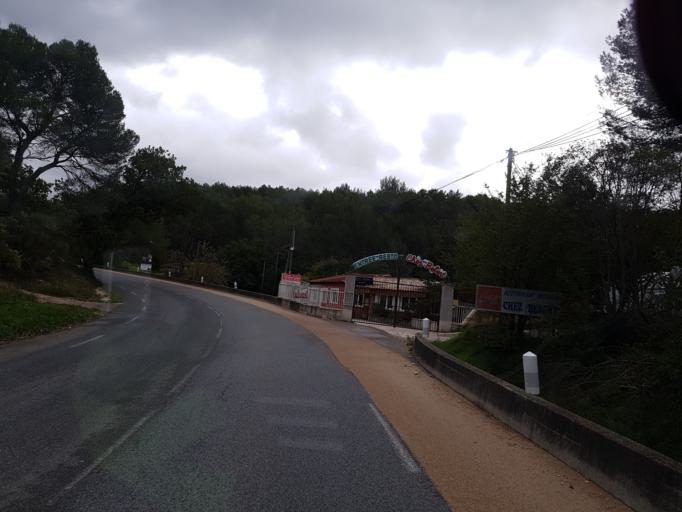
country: FR
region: Provence-Alpes-Cote d'Azur
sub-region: Departement des Bouches-du-Rhone
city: Cuges-les-Pins
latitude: 43.2649
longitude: 5.7405
